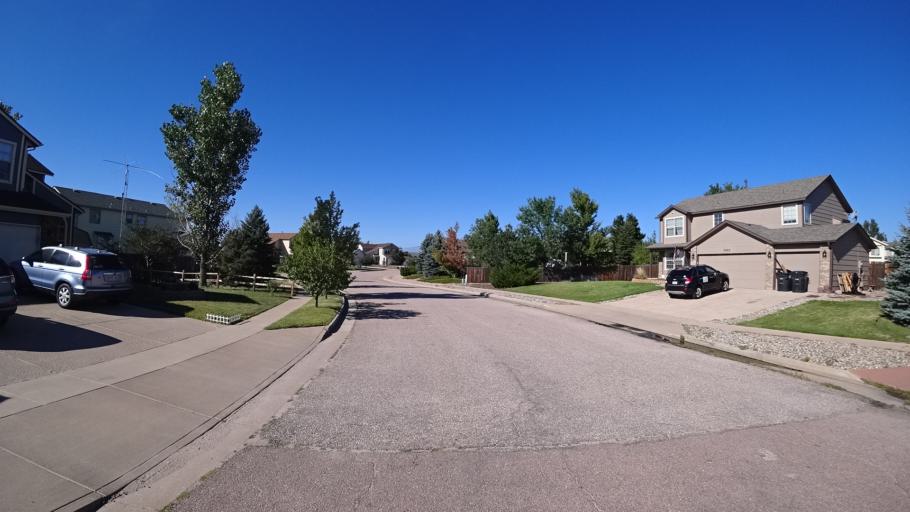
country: US
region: Colorado
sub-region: El Paso County
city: Black Forest
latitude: 38.9475
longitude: -104.7338
